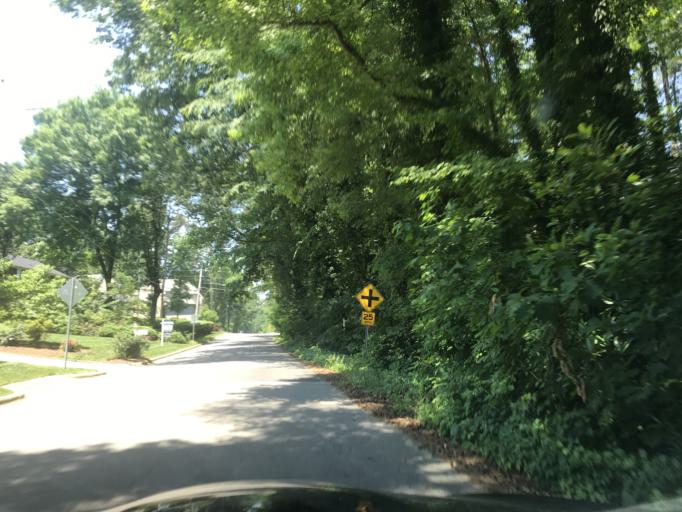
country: US
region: North Carolina
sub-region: Wake County
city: West Raleigh
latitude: 35.8332
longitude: -78.6584
